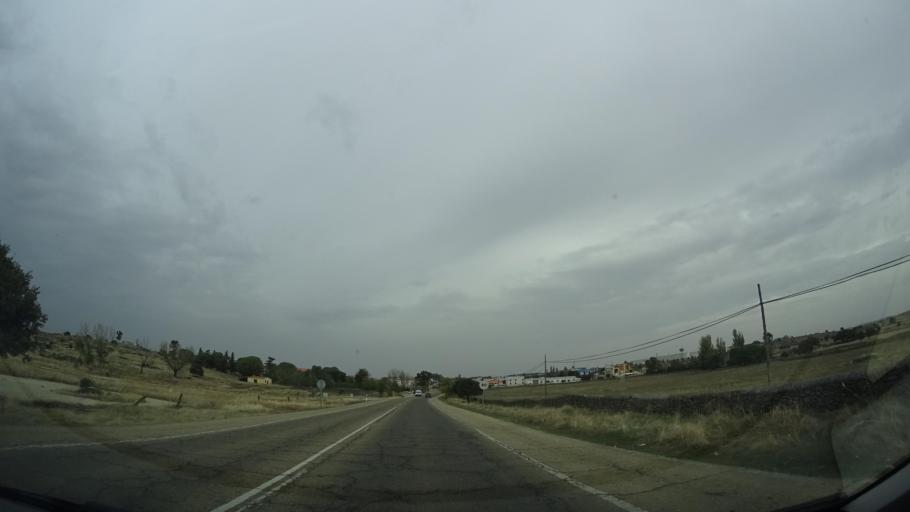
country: ES
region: Extremadura
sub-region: Provincia de Caceres
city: Trujillo
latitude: 39.4715
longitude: -5.8612
